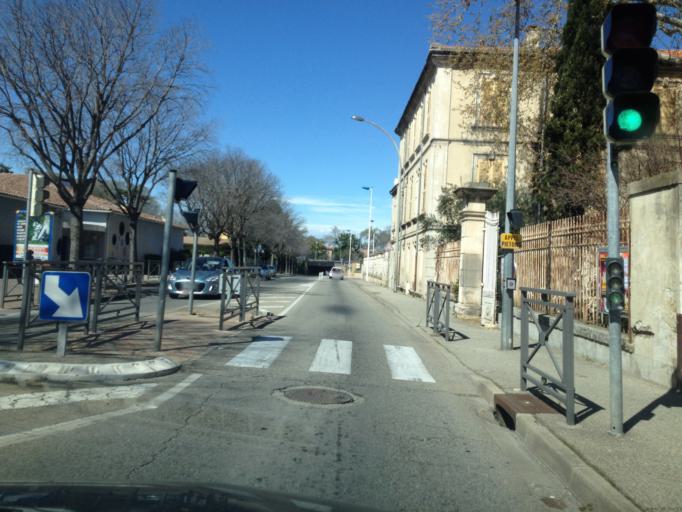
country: FR
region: Provence-Alpes-Cote d'Azur
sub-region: Departement du Vaucluse
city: Sorgues
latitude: 44.0047
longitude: 4.8770
